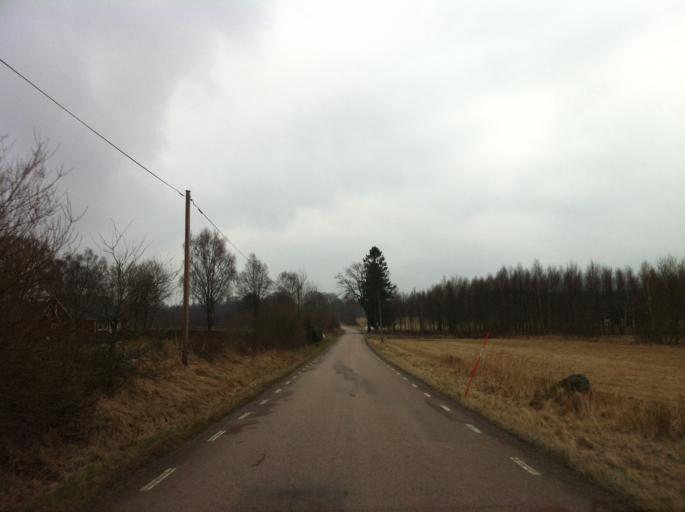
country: SE
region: Skane
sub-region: Svalovs Kommun
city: Kagerod
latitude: 56.0147
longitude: 13.1642
